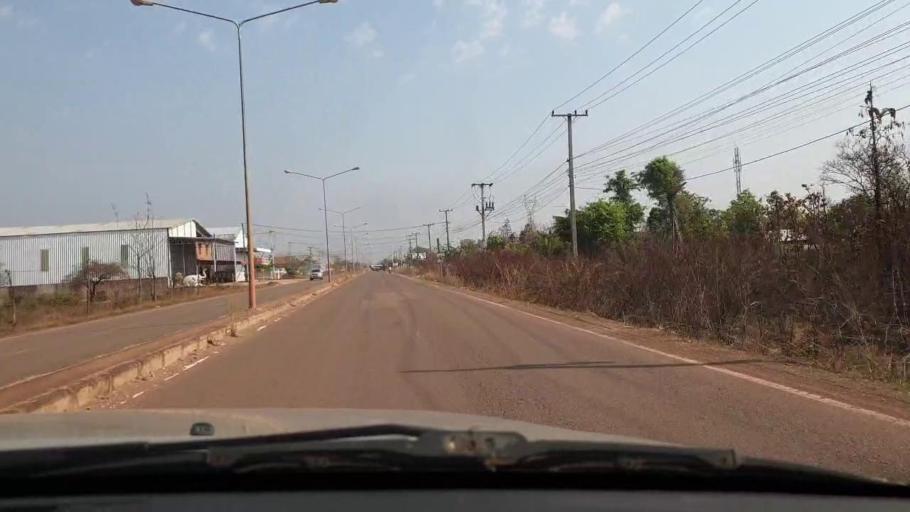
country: LA
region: Vientiane
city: Vientiane
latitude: 18.0074
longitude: 102.7207
